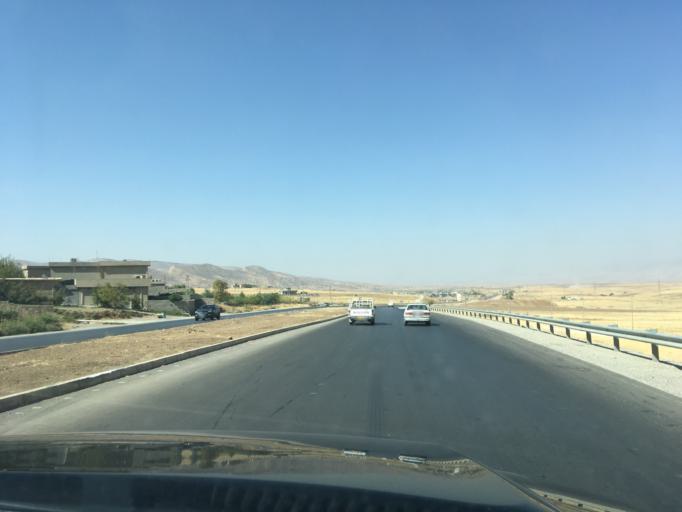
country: IQ
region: Arbil
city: Shaqlawah
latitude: 36.4920
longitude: 44.3724
